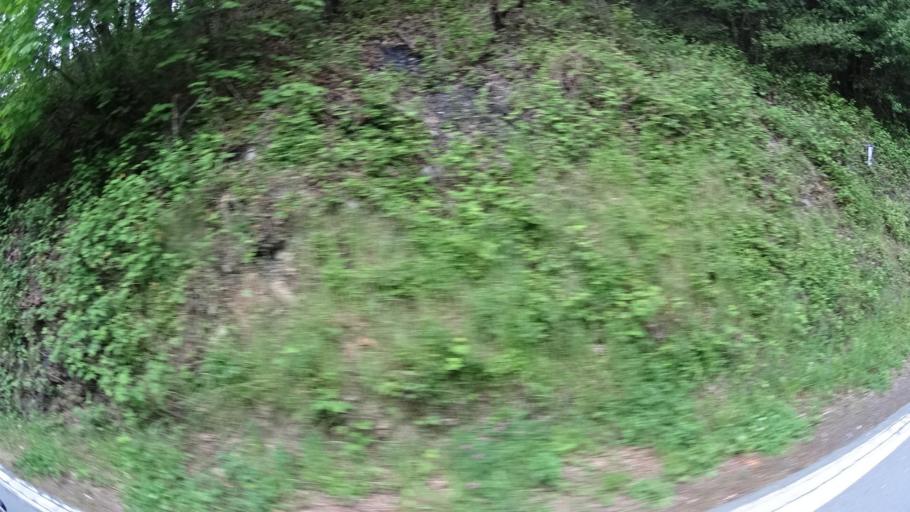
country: US
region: California
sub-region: Humboldt County
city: Willow Creek
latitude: 41.1921
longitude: -123.7145
